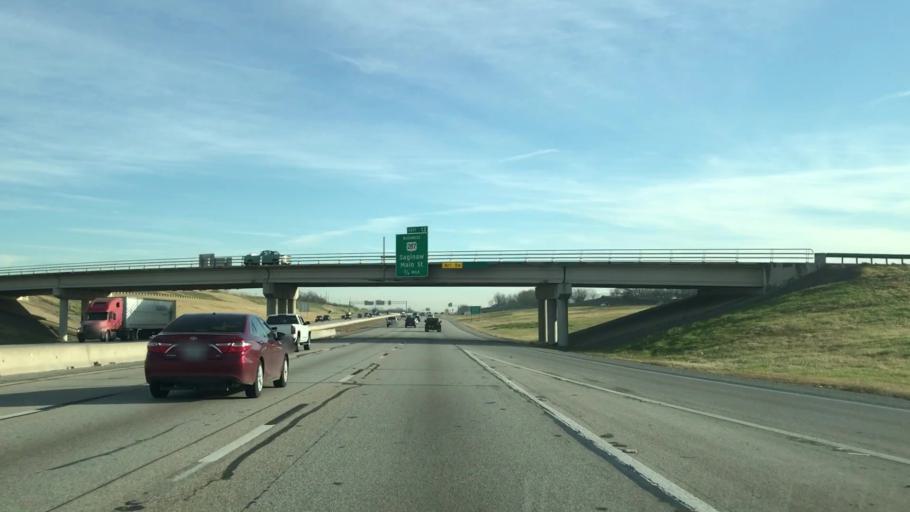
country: US
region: Texas
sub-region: Tarrant County
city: Sansom Park
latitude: 32.8291
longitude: -97.3801
